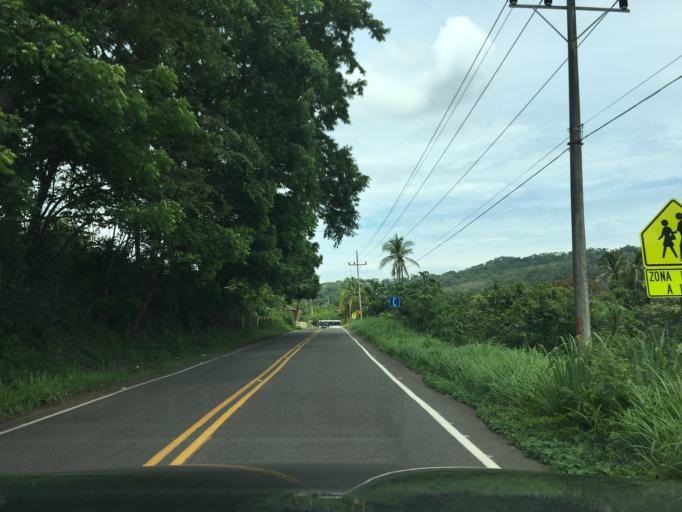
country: CR
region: Puntarenas
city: Esparza
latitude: 9.9318
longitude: -84.6931
